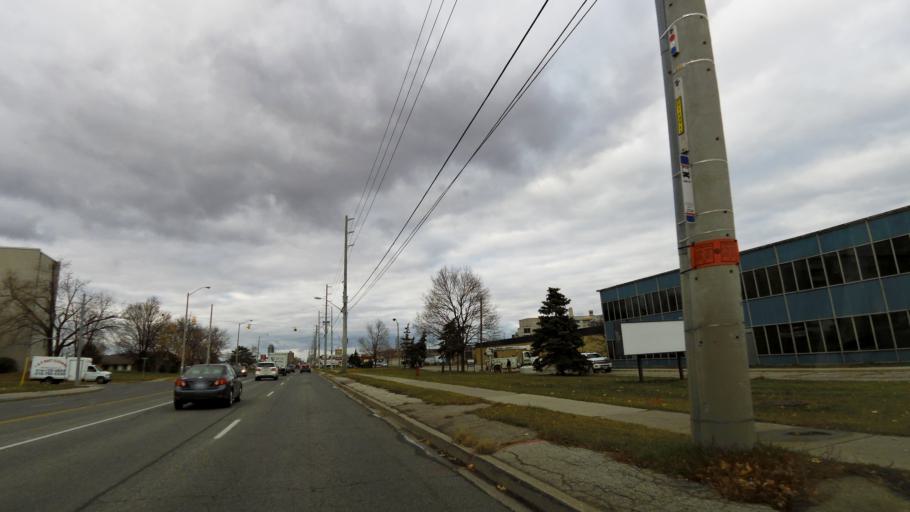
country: CA
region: Ontario
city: Brampton
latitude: 43.6841
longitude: -79.7339
